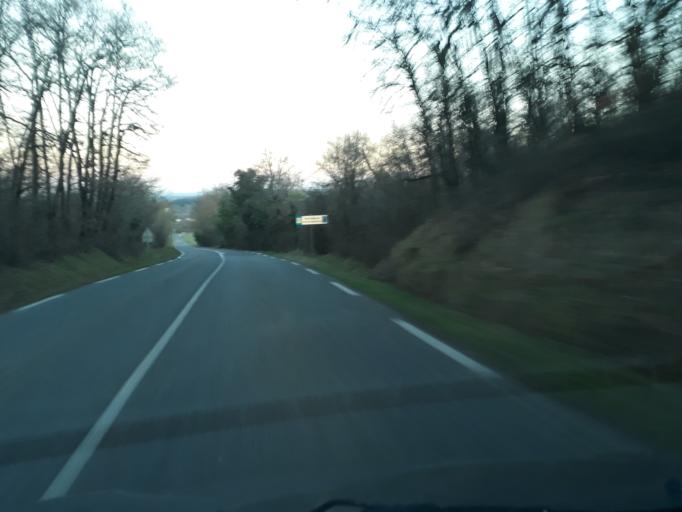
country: FR
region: Midi-Pyrenees
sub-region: Departement du Gers
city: Pujaudran
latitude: 43.5557
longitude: 1.1375
